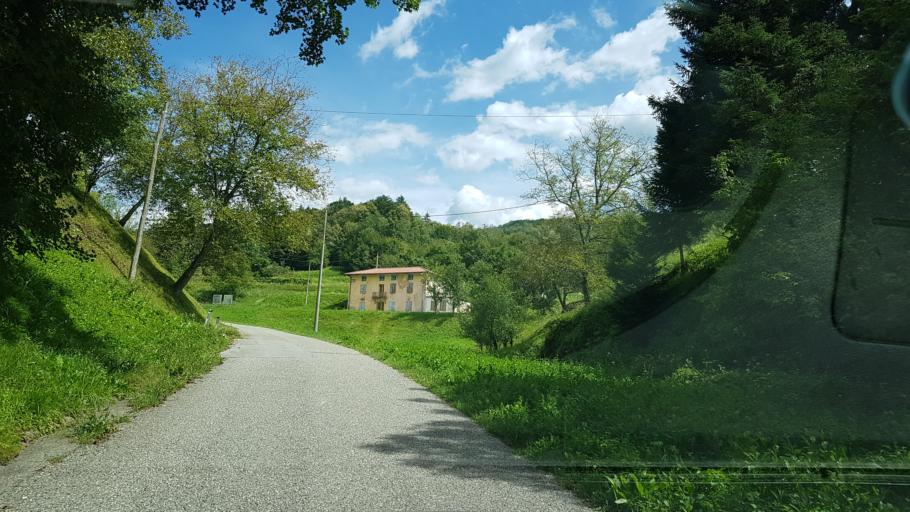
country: IT
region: Friuli Venezia Giulia
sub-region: Provincia di Udine
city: Stregna
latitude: 46.0991
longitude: 13.5854
